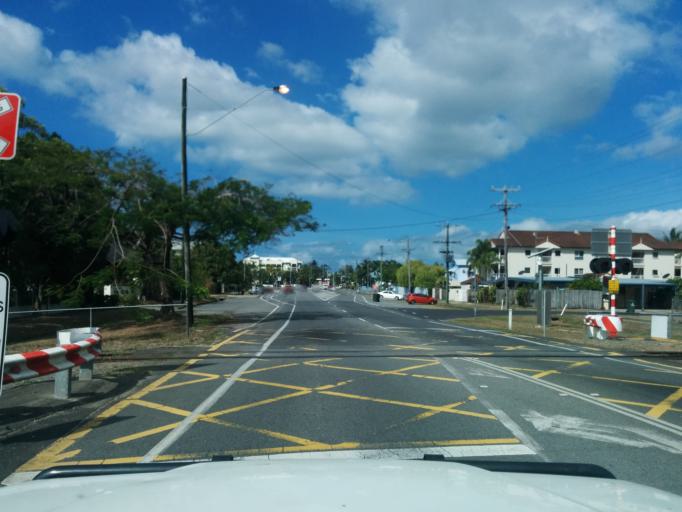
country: AU
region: Queensland
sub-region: Cairns
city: Cairns
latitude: -16.9101
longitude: 145.7585
